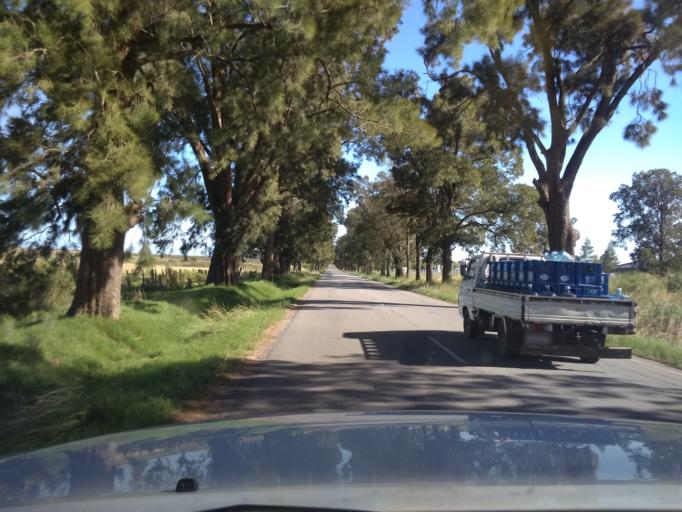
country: UY
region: Canelones
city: San Bautista
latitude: -34.3930
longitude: -55.9596
